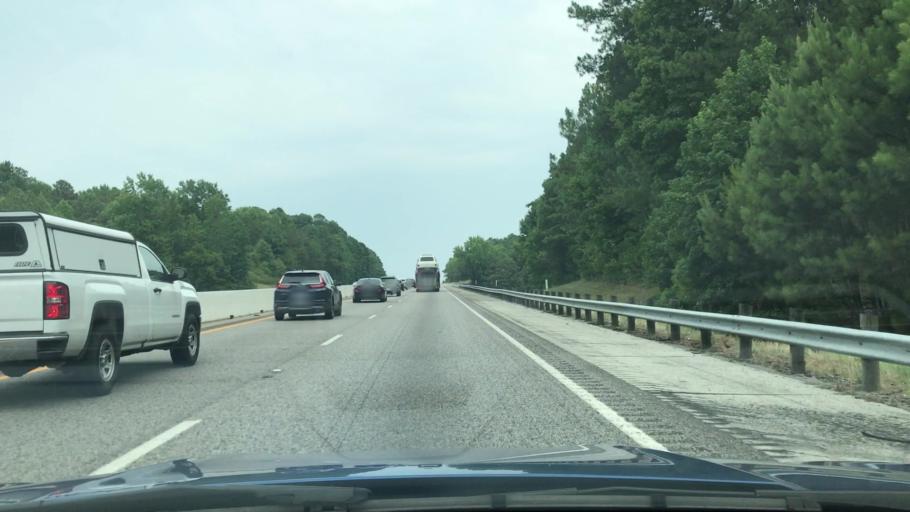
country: US
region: Texas
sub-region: Smith County
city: Lindale
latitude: 32.4659
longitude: -95.3363
